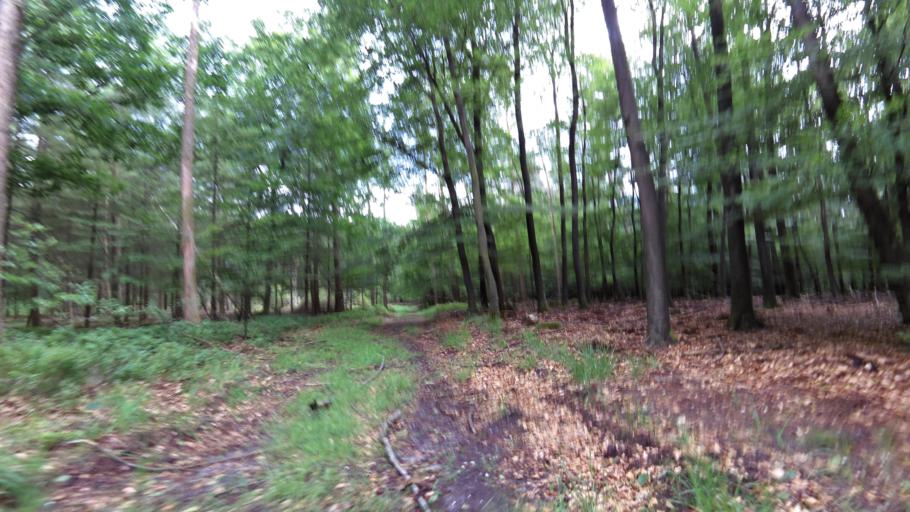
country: NL
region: Gelderland
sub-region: Gemeente Apeldoorn
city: Apeldoorn
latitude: 52.2230
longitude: 5.8931
